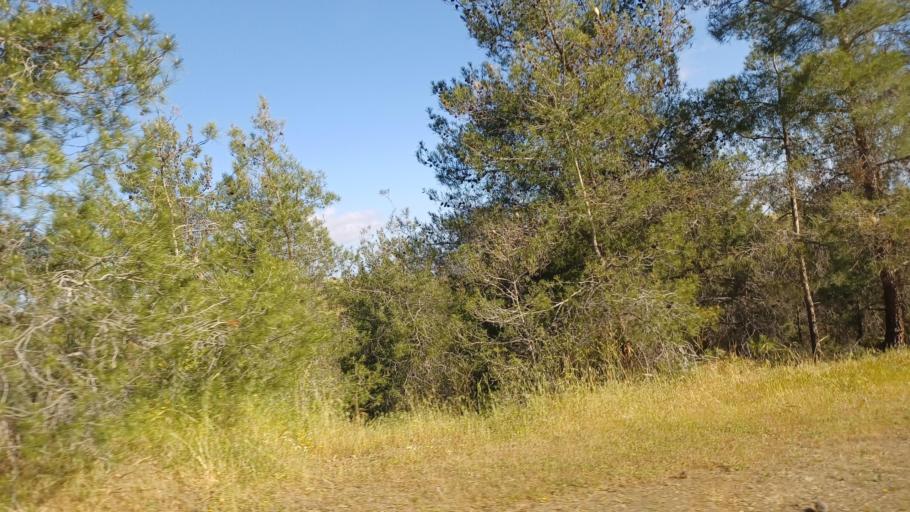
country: CY
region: Lefkosia
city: Peristerona
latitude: 35.0289
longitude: 33.0553
